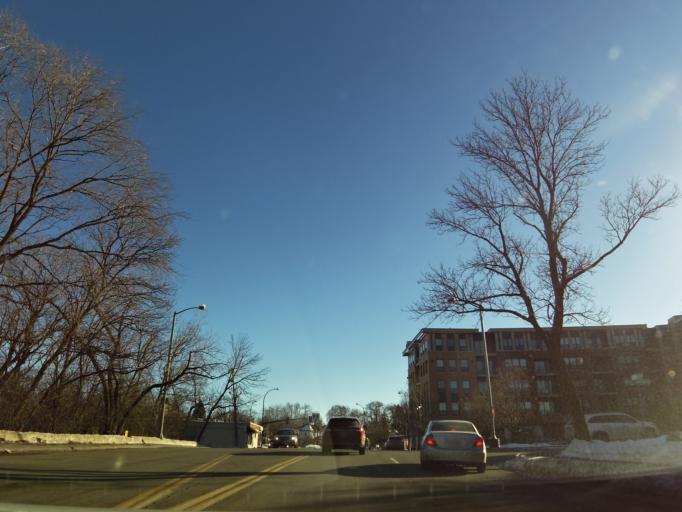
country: US
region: Minnesota
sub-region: Hennepin County
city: Saint Louis Park
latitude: 44.9353
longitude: -93.3378
